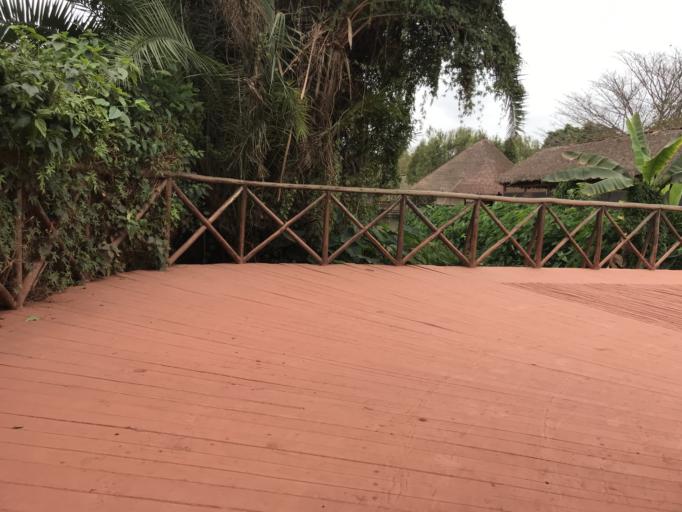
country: PE
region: Callao
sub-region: Callao
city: Callao
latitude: -12.0707
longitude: -77.0850
